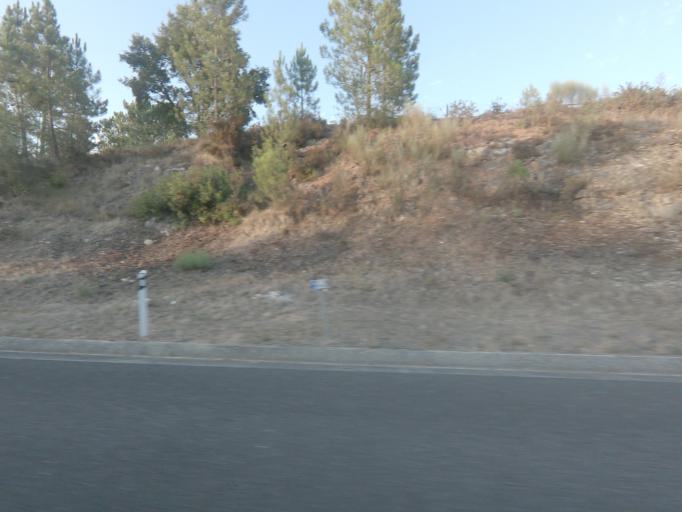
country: PT
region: Leiria
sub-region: Leiria
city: Santa Catarina da Serra
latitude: 39.7044
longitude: -8.7037
